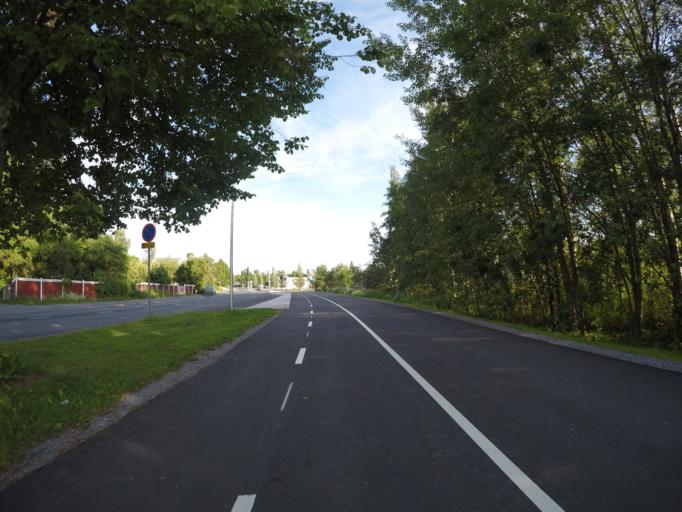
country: FI
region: Haeme
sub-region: Haemeenlinna
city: Haemeenlinna
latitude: 60.9884
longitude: 24.4391
